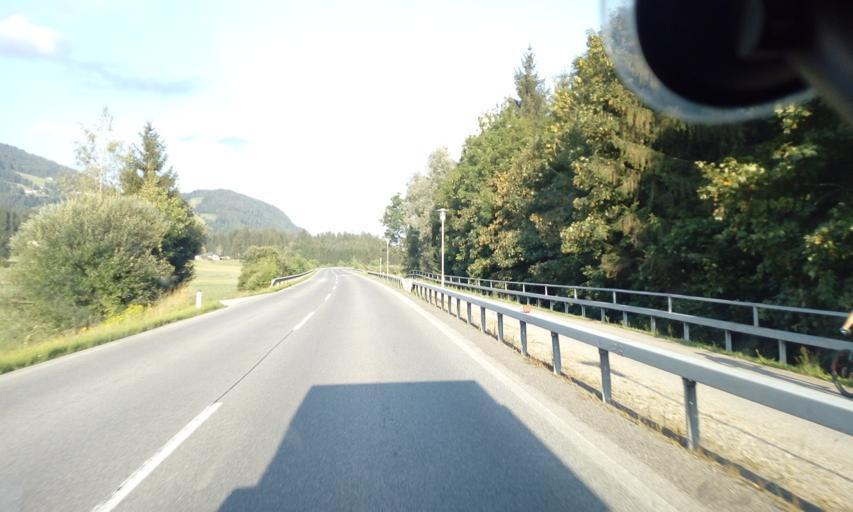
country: AT
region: Carinthia
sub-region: Politischer Bezirk Spittal an der Drau
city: Irschen
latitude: 46.7418
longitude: 13.0173
